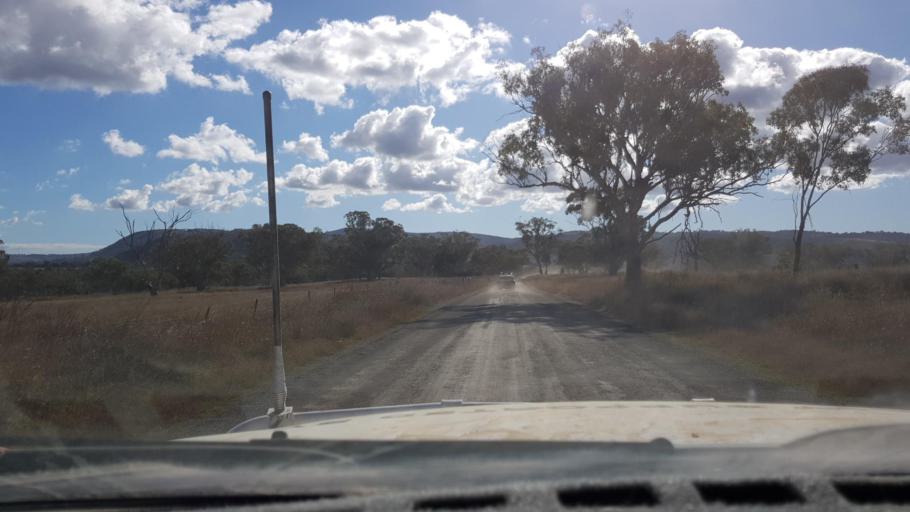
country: AU
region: New South Wales
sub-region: Tamworth Municipality
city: Manilla
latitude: -30.6303
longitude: 150.5085
